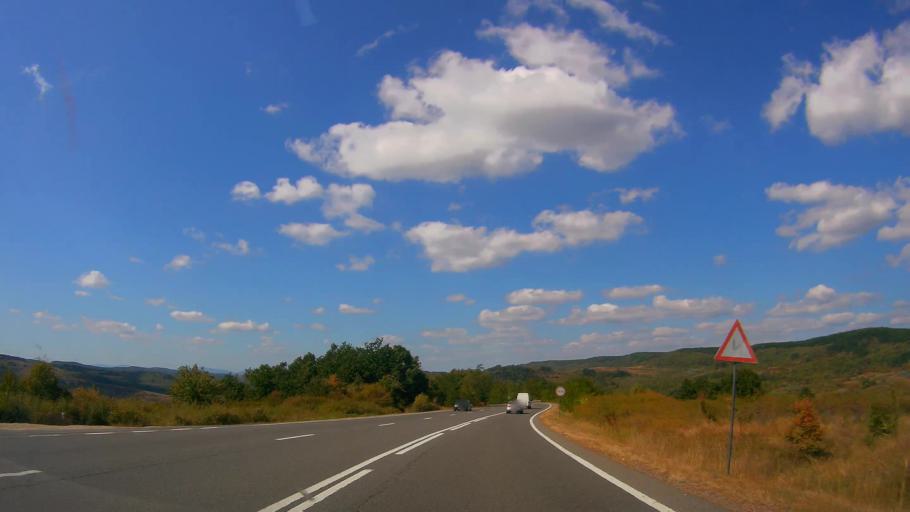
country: RO
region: Cluj
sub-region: Comuna Sanpaul
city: Sanpaul
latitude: 46.9459
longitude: 23.3781
